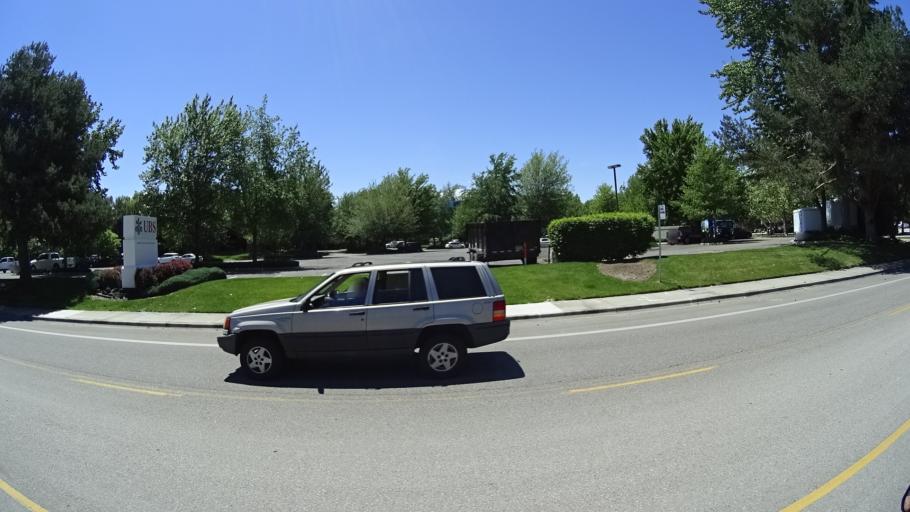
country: US
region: Idaho
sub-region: Ada County
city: Boise
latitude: 43.6131
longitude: -116.2132
